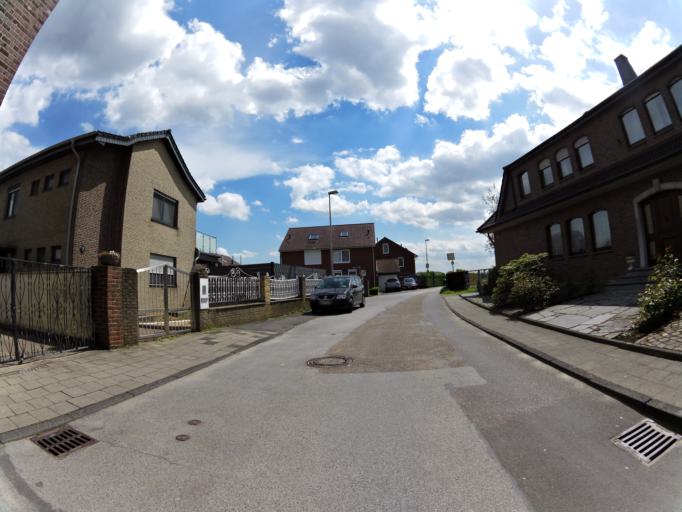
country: DE
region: North Rhine-Westphalia
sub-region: Regierungsbezirk Koln
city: Ubach-Palenberg
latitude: 50.9035
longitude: 6.1383
